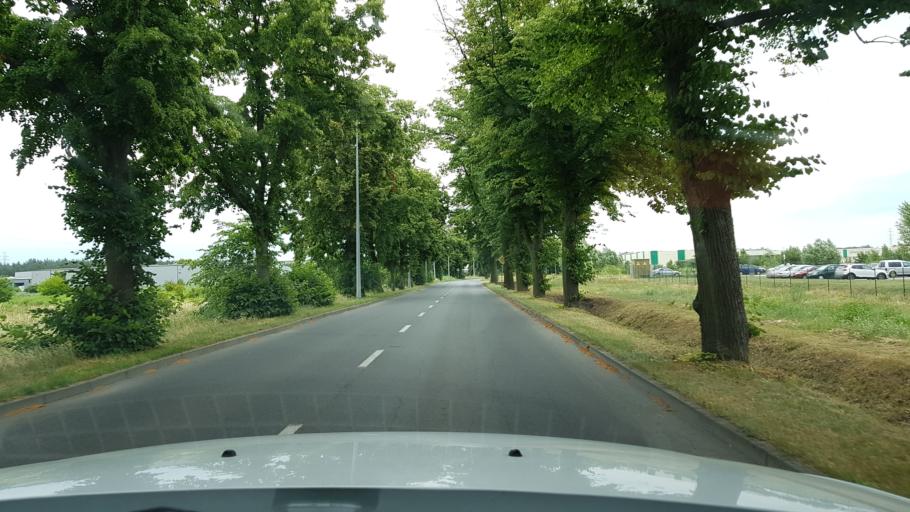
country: PL
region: Lubusz
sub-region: Powiat gorzowski
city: Kostrzyn nad Odra
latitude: 52.6073
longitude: 14.6198
